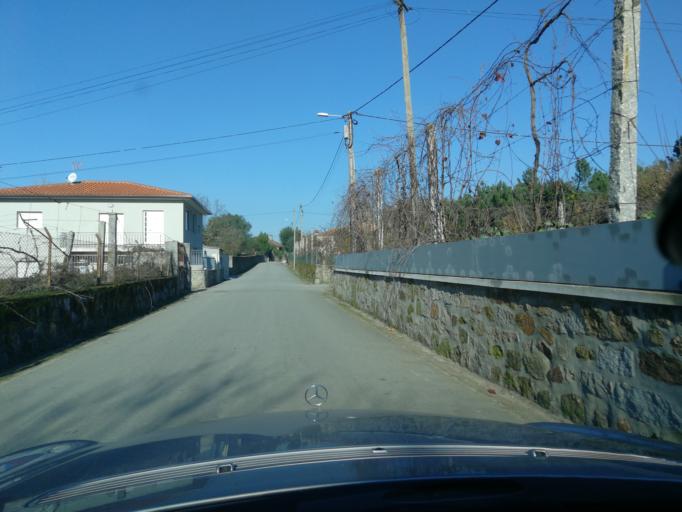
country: PT
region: Braga
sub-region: Braga
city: Adaufe
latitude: 41.6151
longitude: -8.3978
